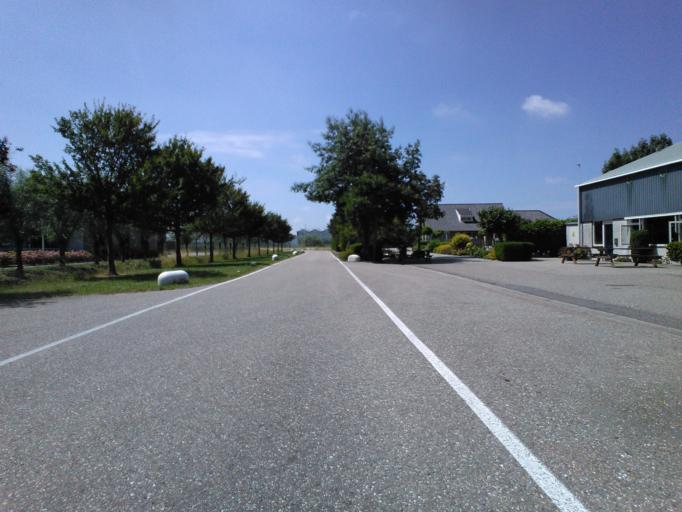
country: NL
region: South Holland
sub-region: Gemeente Westland
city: De Lier
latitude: 51.9641
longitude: 4.2620
